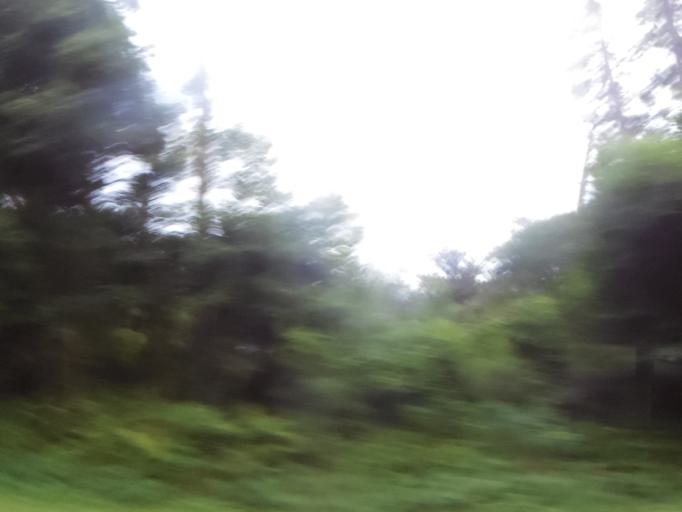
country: US
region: Florida
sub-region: Duval County
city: Jacksonville
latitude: 30.2594
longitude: -81.6978
